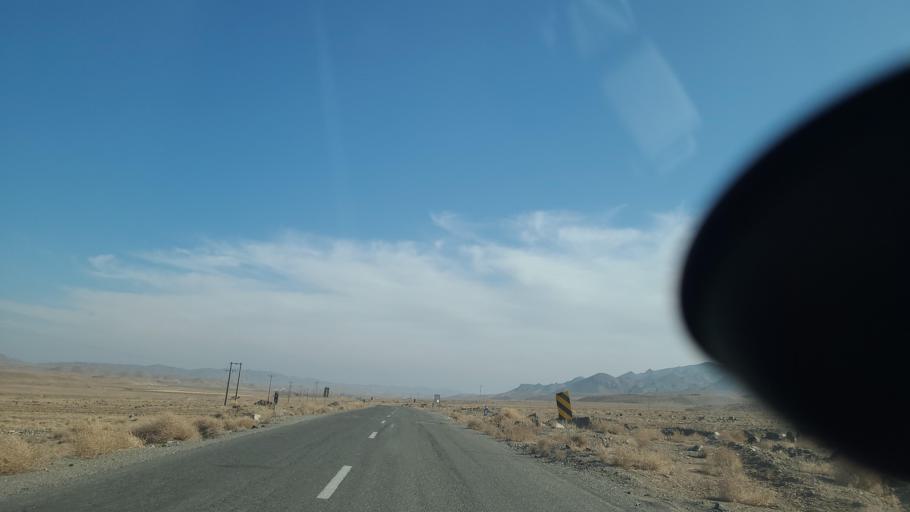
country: IR
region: Razavi Khorasan
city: Fariman
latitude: 35.5870
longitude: 59.6467
